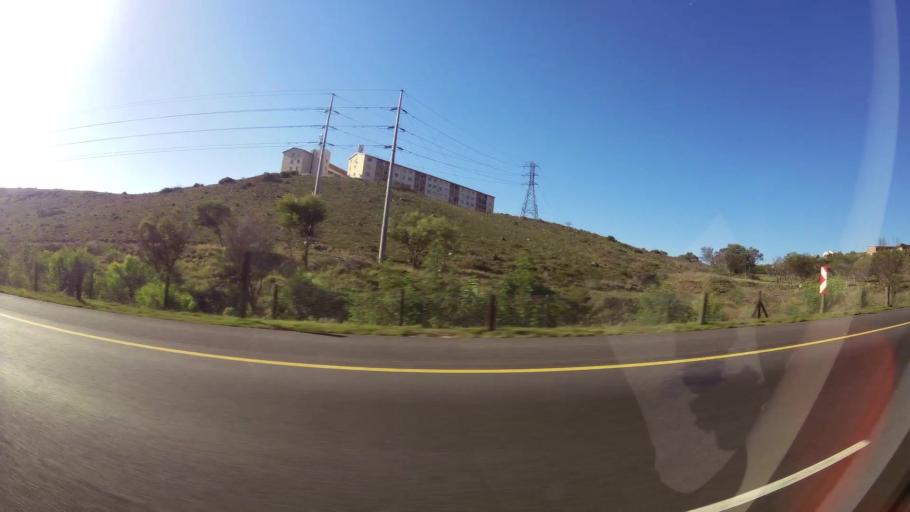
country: ZA
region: Eastern Cape
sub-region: Nelson Mandela Bay Metropolitan Municipality
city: Port Elizabeth
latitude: -33.9345
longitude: 25.5572
